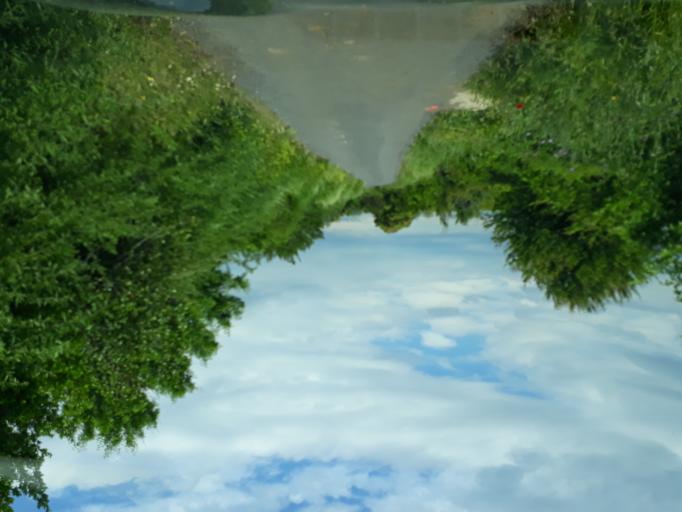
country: FR
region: Languedoc-Roussillon
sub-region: Departement de l'Herault
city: Agde
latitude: 43.2900
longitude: 3.4903
